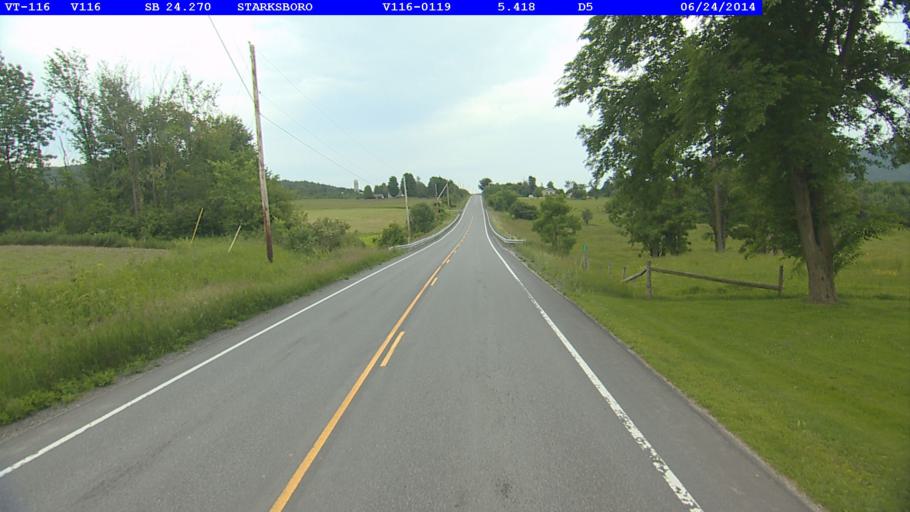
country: US
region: Vermont
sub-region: Chittenden County
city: Hinesburg
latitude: 44.2623
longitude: -73.0650
